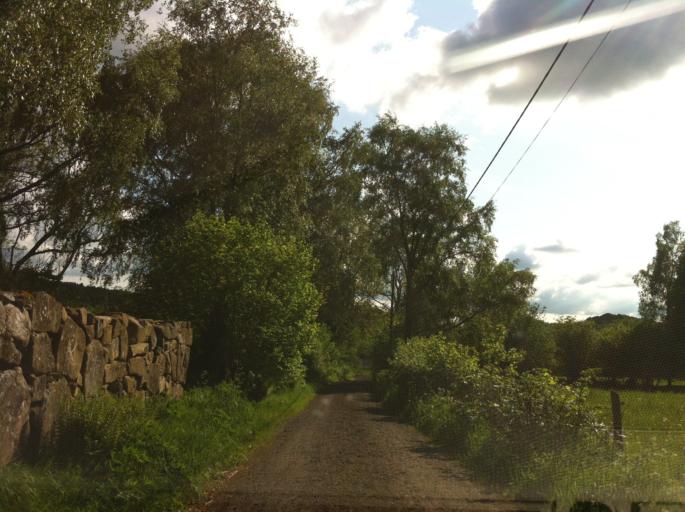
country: SE
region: Skane
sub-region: Klippans Kommun
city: Ljungbyhed
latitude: 56.0363
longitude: 13.2187
